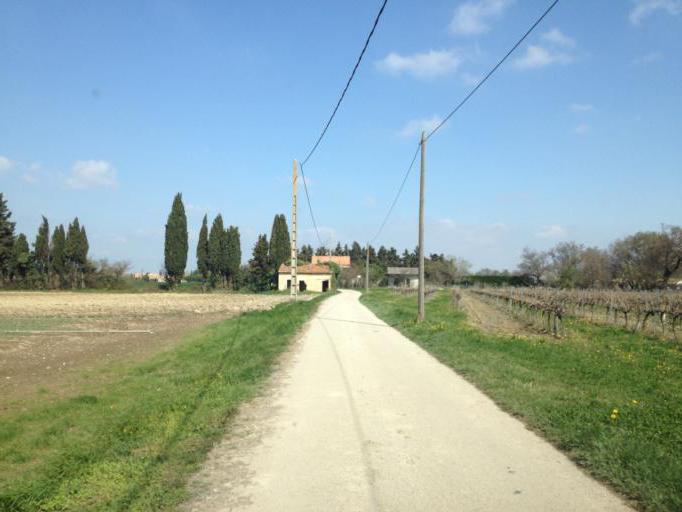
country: FR
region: Provence-Alpes-Cote d'Azur
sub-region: Departement du Vaucluse
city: Jonquieres
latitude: 44.1059
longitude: 4.9042
